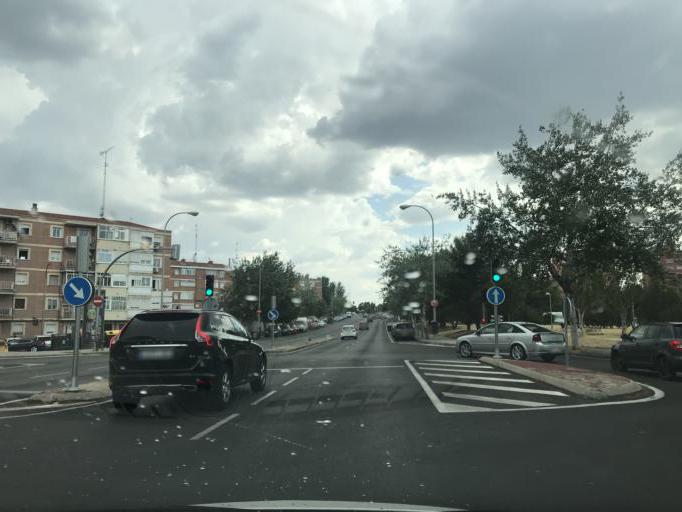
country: ES
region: Madrid
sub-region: Provincia de Madrid
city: Pinar de Chamartin
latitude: 40.4734
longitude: -3.6563
